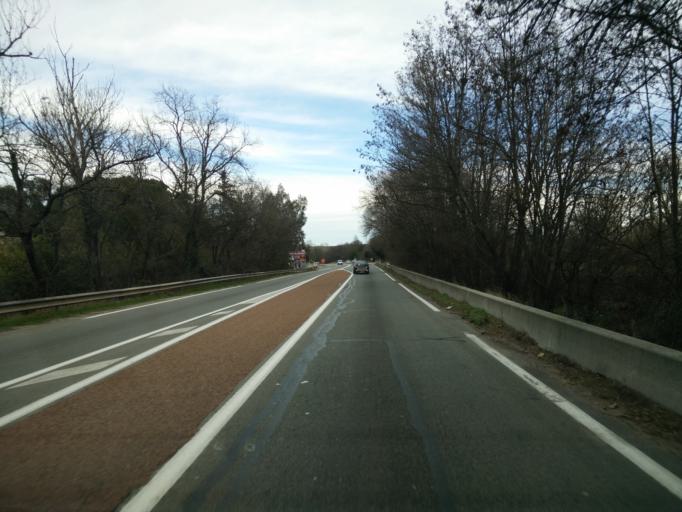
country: FR
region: Provence-Alpes-Cote d'Azur
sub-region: Departement du Var
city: Le Muy
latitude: 43.4677
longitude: 6.6007
